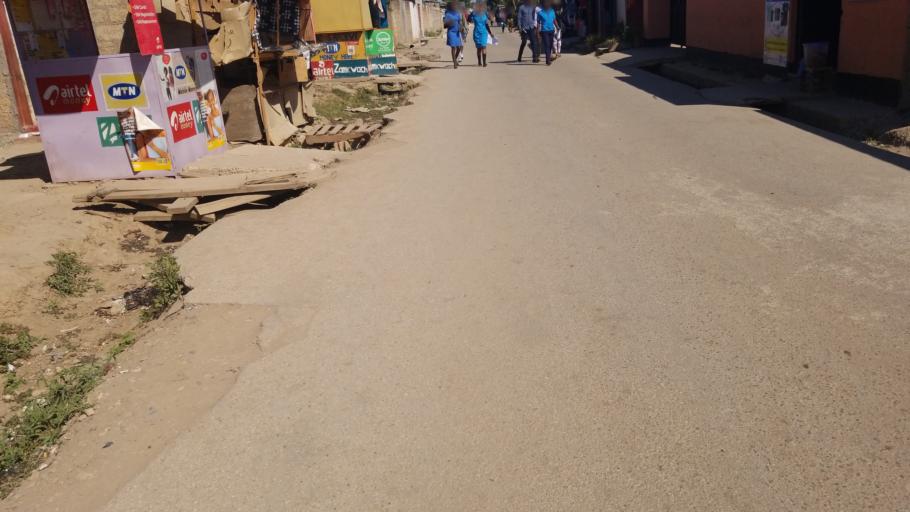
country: ZM
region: Lusaka
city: Lusaka
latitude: -15.4012
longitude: 28.3299
